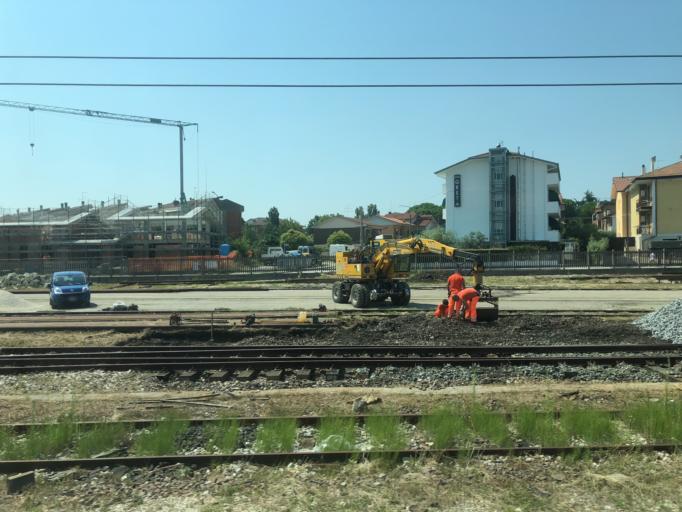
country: IT
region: Emilia-Romagna
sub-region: Provincia di Rimini
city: Santarcangelo
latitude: 44.0702
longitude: 12.4509
